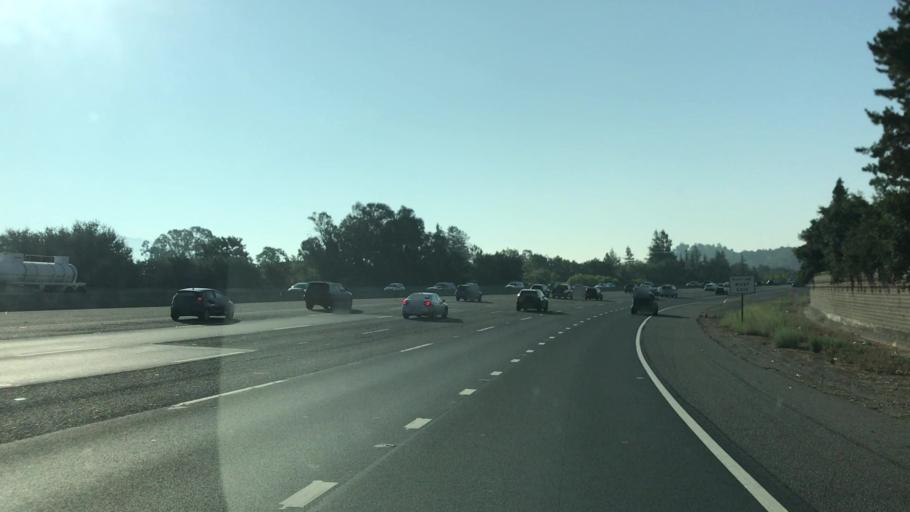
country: US
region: California
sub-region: Contra Costa County
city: Walnut Creek
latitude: 37.8900
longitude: -122.0593
